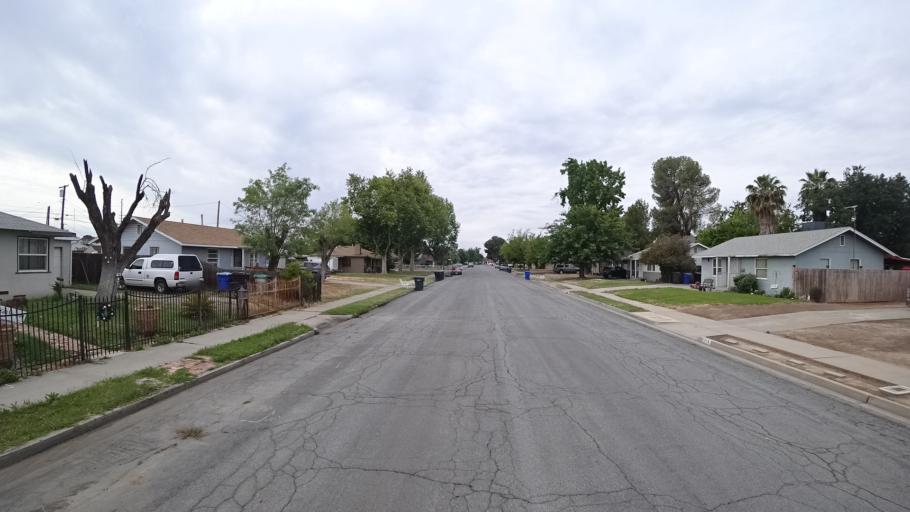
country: US
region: California
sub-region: Kings County
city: Hanford
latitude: 36.3397
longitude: -119.6563
